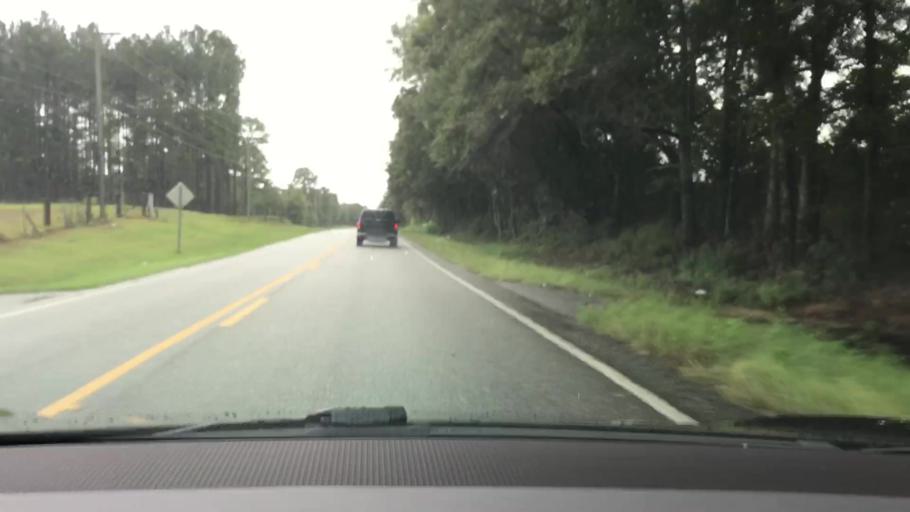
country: US
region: Alabama
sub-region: Geneva County
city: Samson
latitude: 31.1106
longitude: -86.1112
